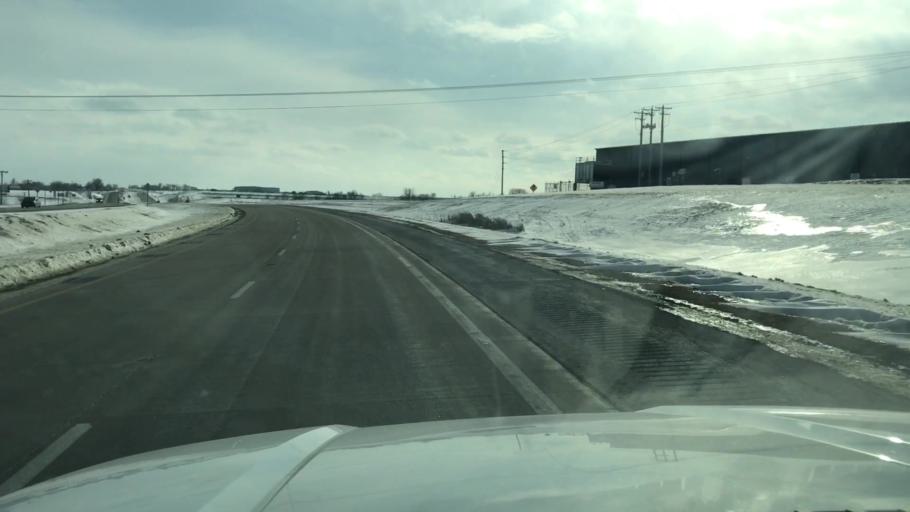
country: US
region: Missouri
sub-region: Nodaway County
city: Maryville
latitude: 40.3118
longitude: -94.8743
